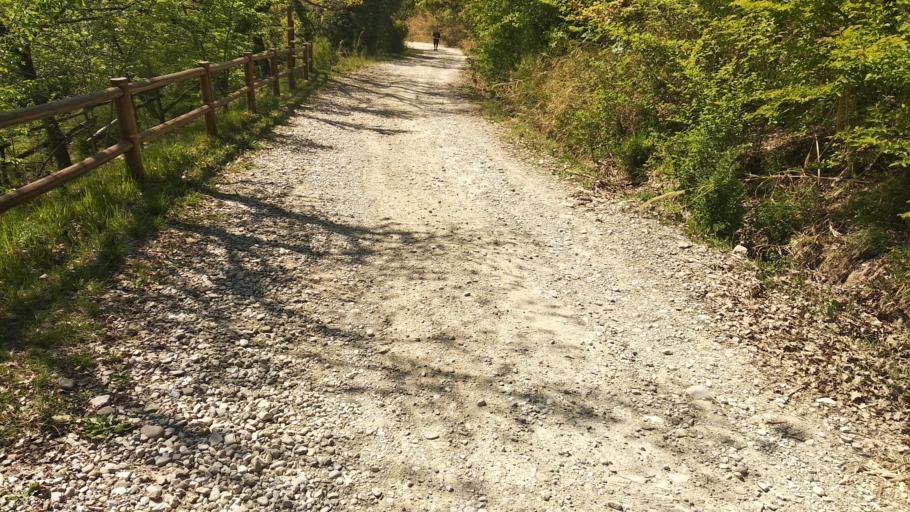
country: IT
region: Emilia-Romagna
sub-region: Provincia di Ravenna
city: Riolo Terme
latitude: 44.2356
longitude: 11.6936
